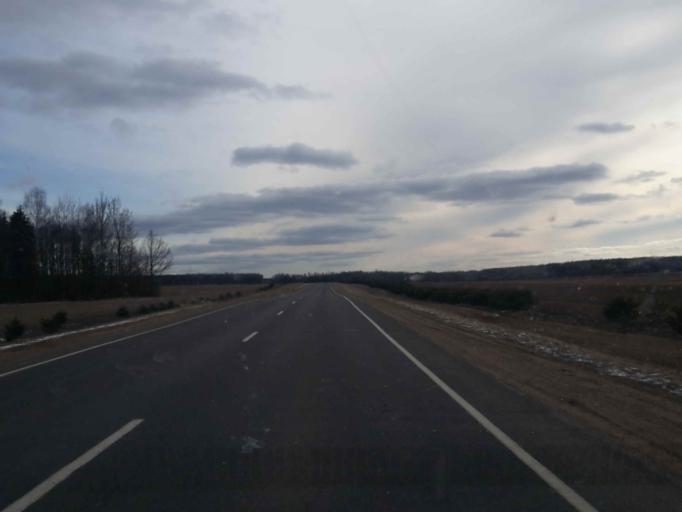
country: BY
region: Minsk
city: Kryvichy
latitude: 54.6461
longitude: 27.1722
